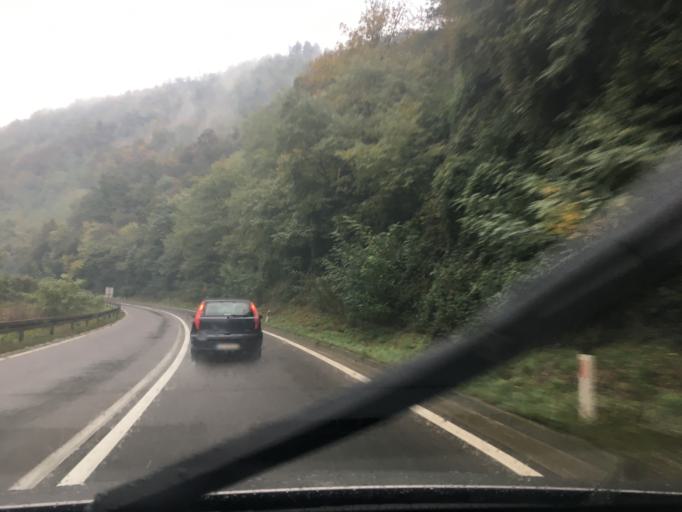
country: RS
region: Central Serbia
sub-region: Pcinjski Okrug
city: Vladicin Han
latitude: 42.7429
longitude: 22.0636
